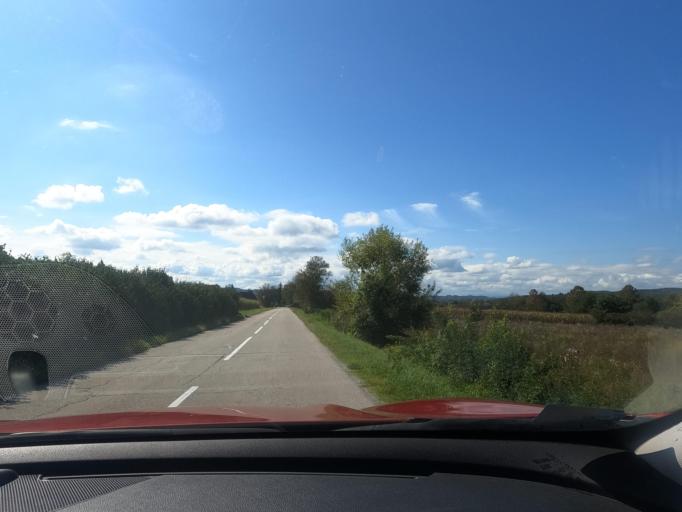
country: BA
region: Federation of Bosnia and Herzegovina
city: Vrnograc
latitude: 45.2621
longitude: 15.9502
